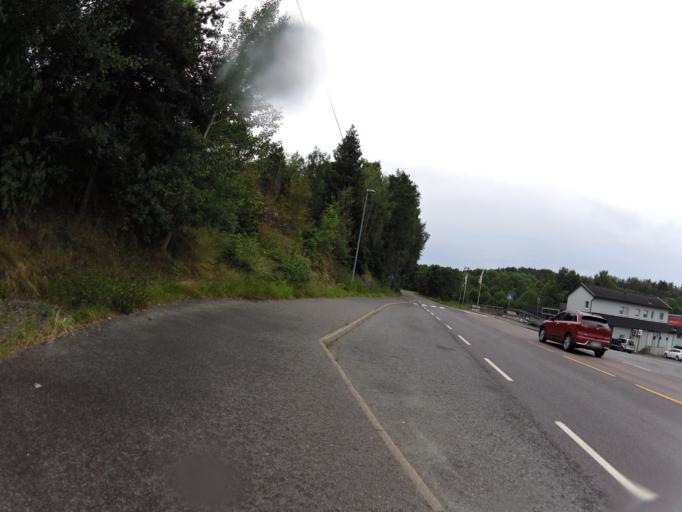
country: NO
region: Ostfold
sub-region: Moss
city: Moss
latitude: 59.4719
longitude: 10.6915
